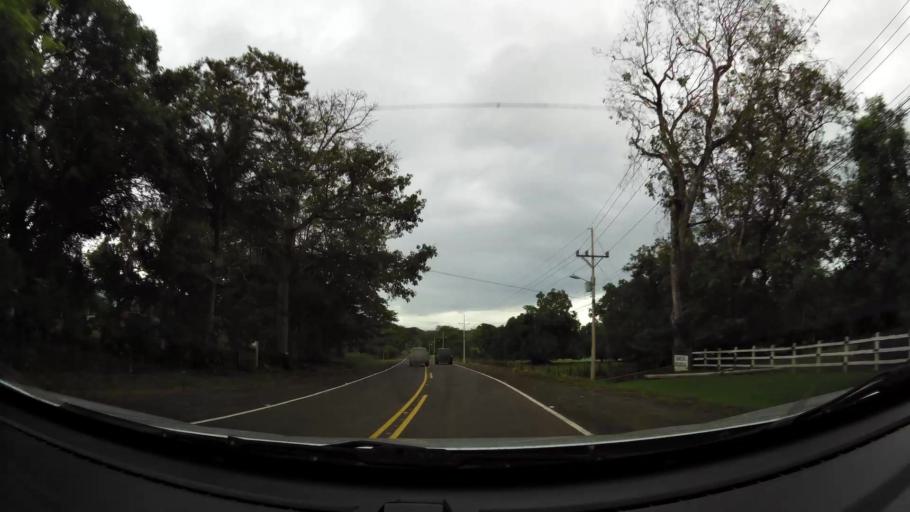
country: CR
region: Alajuela
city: Orotina
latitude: 9.9476
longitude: -84.5655
